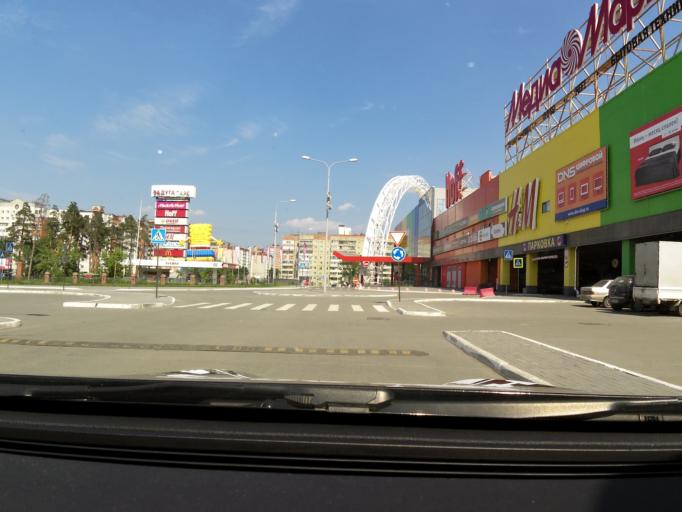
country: RU
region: Sverdlovsk
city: Shirokaya Rechka
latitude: 56.8175
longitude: 60.5363
